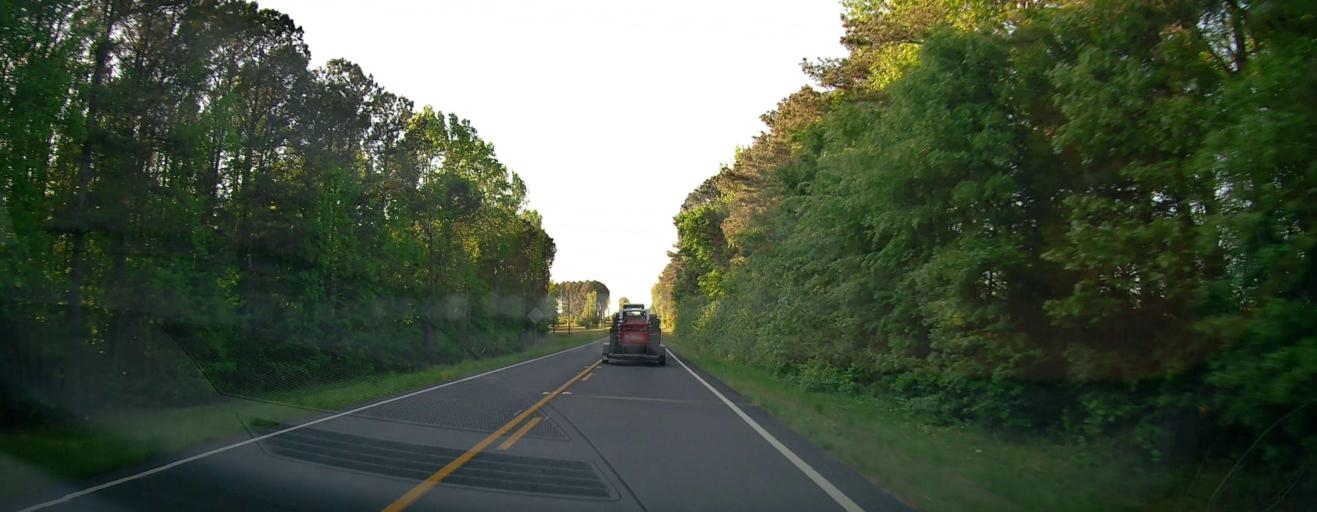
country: US
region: Georgia
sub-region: Walton County
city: Social Circle
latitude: 33.4906
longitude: -83.6500
